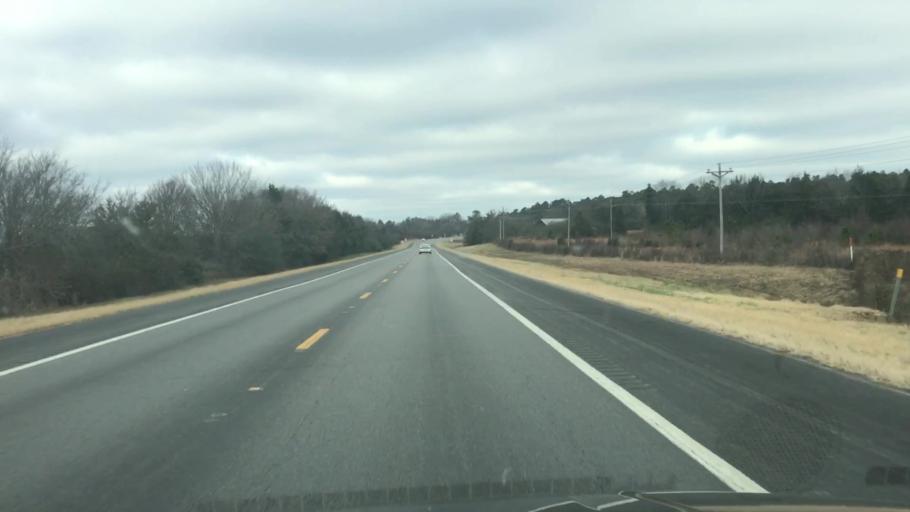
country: US
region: Arkansas
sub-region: Scott County
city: Waldron
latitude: 34.8795
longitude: -94.0992
